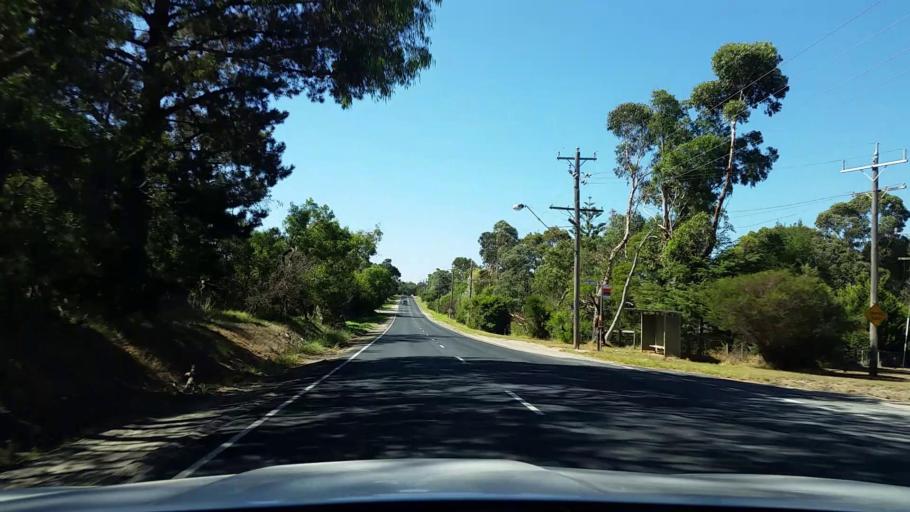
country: AU
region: Victoria
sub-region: Mornington Peninsula
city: Langwarrin South
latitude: -38.1998
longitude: 145.2030
